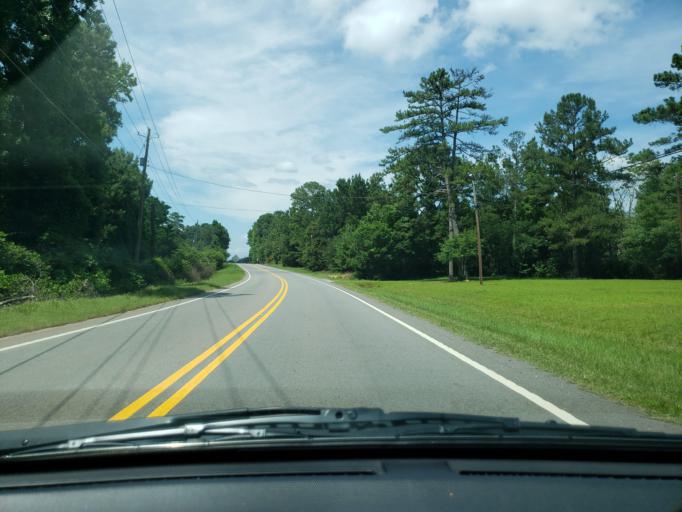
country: US
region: Alabama
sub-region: Elmore County
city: Eclectic
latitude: 32.6787
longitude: -85.9437
